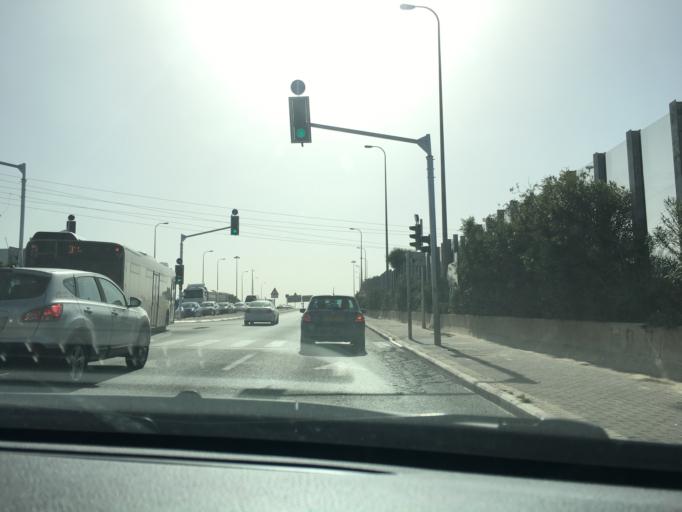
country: IL
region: Central District
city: Kfar Saba
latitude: 32.1673
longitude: 34.9277
